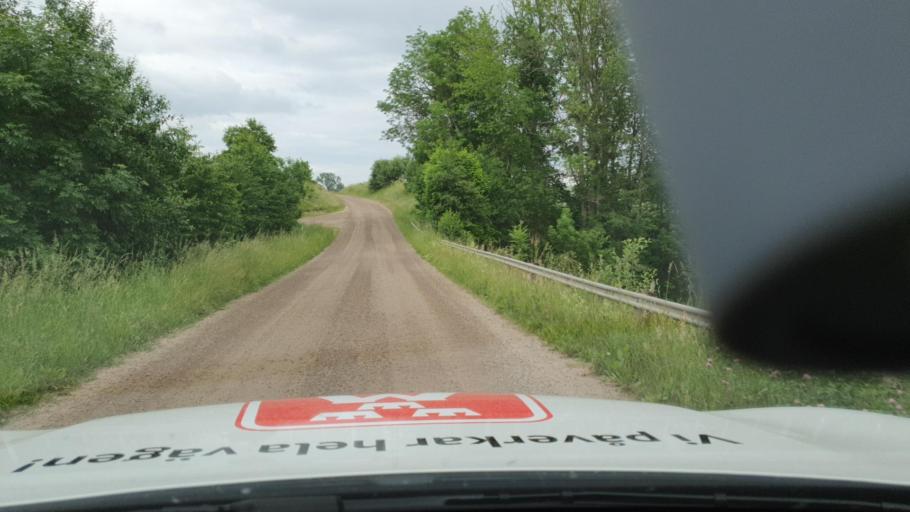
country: SE
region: Vaestra Goetaland
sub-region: Hjo Kommun
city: Hjo
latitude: 58.2092
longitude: 14.1830
